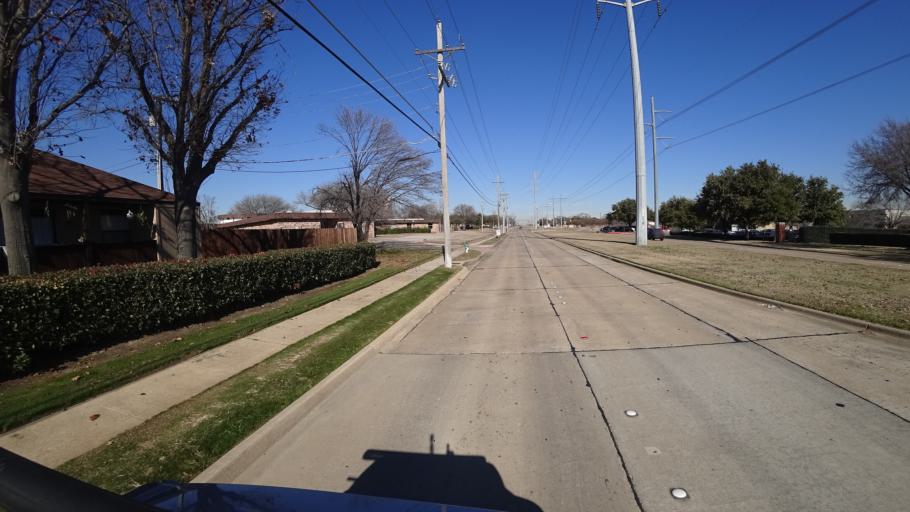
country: US
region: Texas
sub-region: Denton County
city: Lewisville
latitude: 33.0244
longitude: -97.0106
